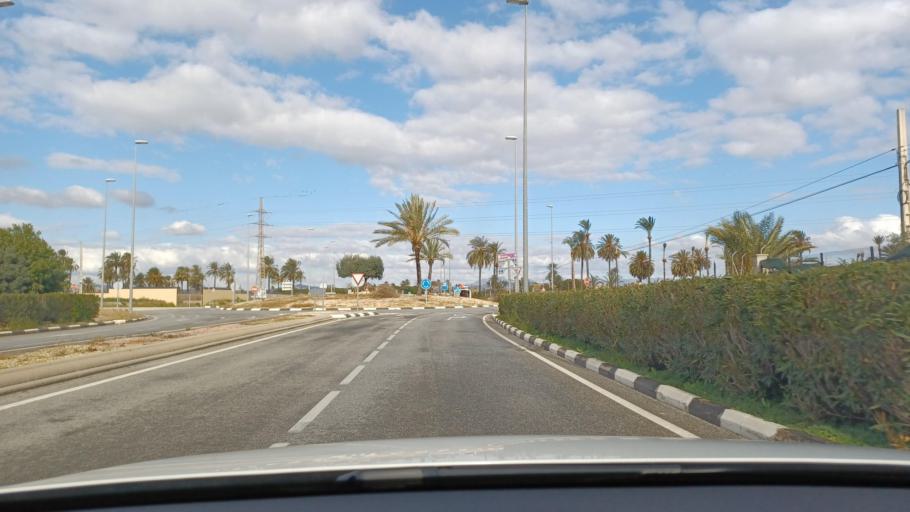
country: ES
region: Valencia
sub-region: Provincia de Alicante
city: Elche
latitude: 38.2309
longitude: -0.6997
